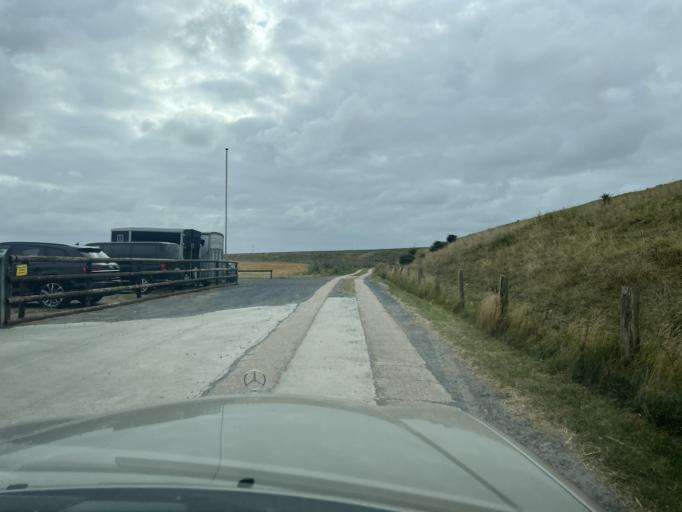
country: DE
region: Schleswig-Holstein
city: Lehe
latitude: 54.3321
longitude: 8.9955
